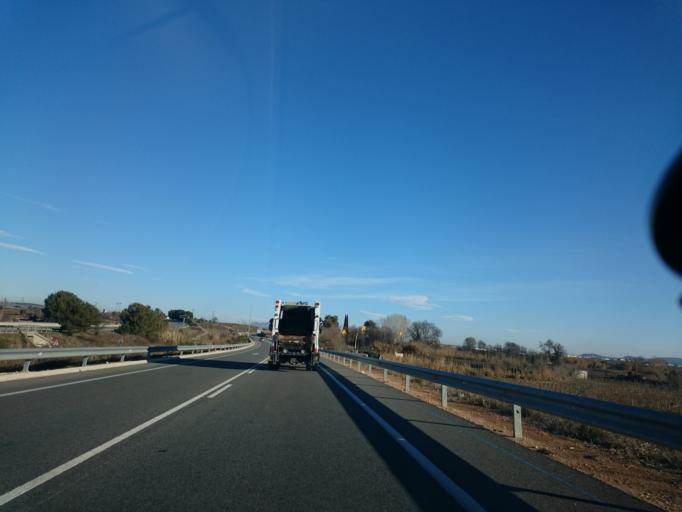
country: ES
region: Catalonia
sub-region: Provincia de Barcelona
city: Vilafranca del Penedes
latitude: 41.3394
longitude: 1.7180
